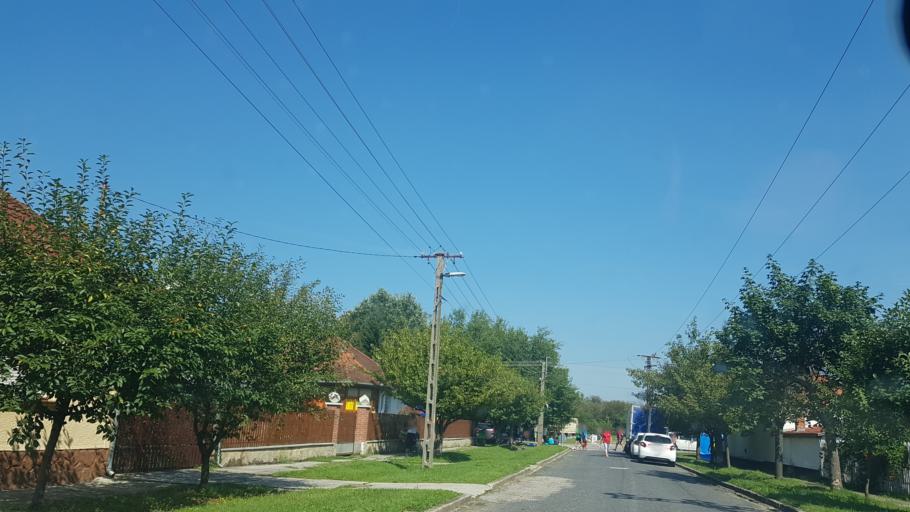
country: HU
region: Somogy
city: Nagyatad
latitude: 46.2357
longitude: 17.3635
